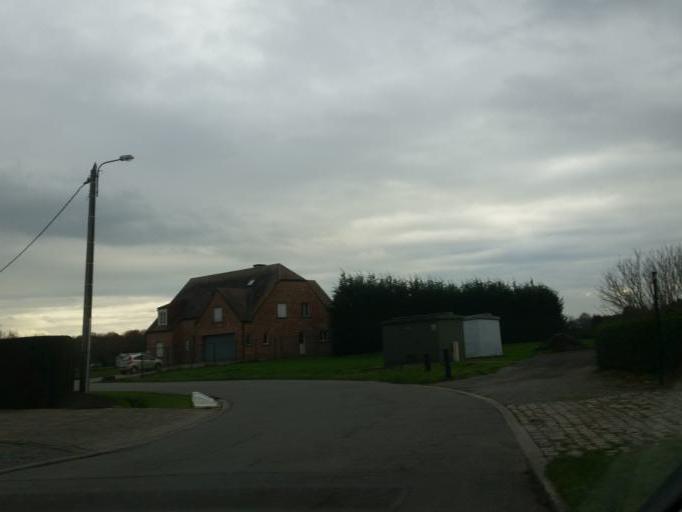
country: BE
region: Flanders
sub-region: Provincie Antwerpen
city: Duffel
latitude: 51.0707
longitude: 4.5066
